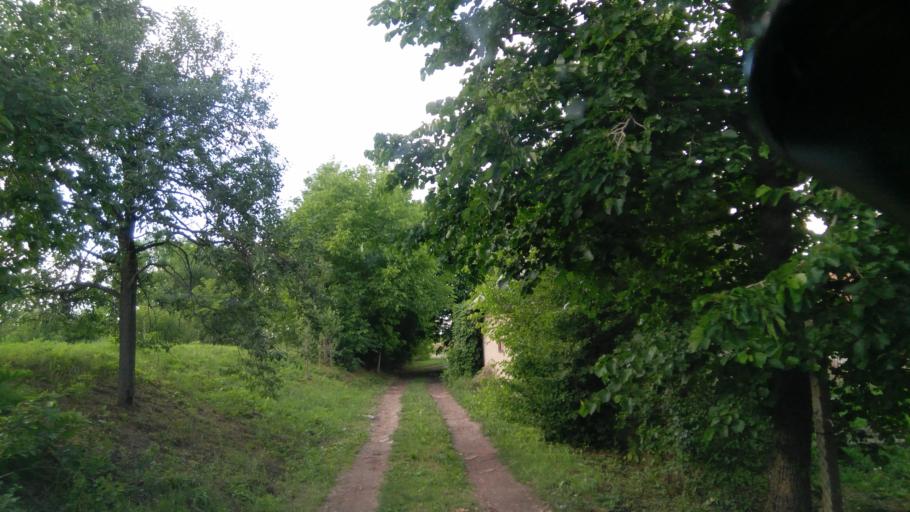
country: HU
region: Bekes
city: Doboz
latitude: 46.7001
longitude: 21.1803
